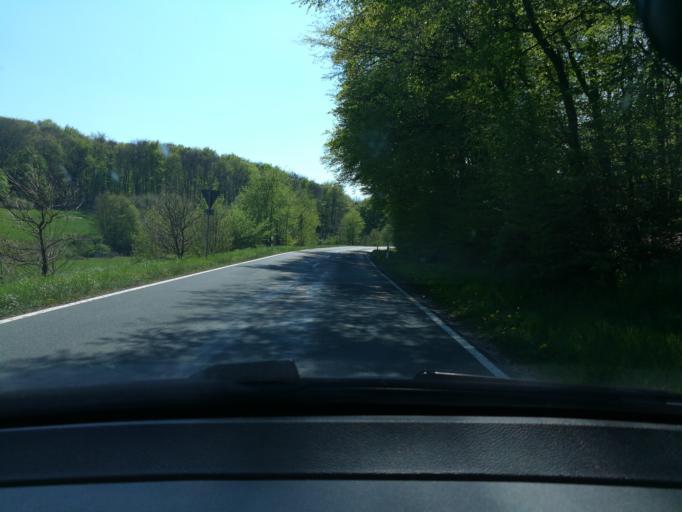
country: DE
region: North Rhine-Westphalia
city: Halle
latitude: 52.0487
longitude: 8.3945
